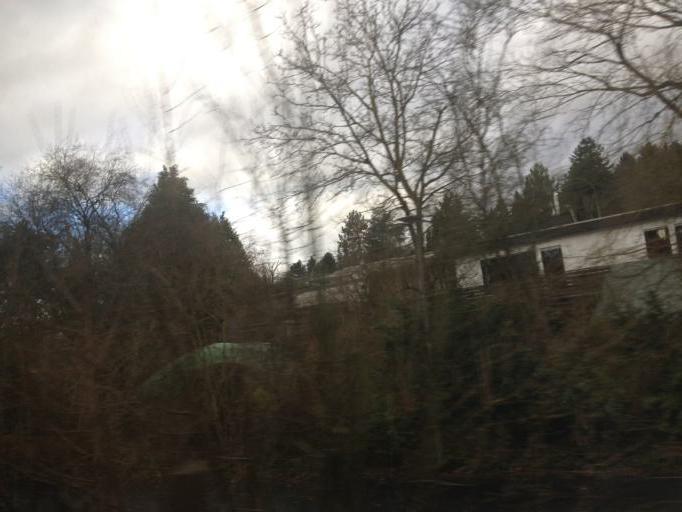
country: DE
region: Hesse
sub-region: Regierungsbezirk Giessen
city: Giessen
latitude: 50.5454
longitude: 8.7249
